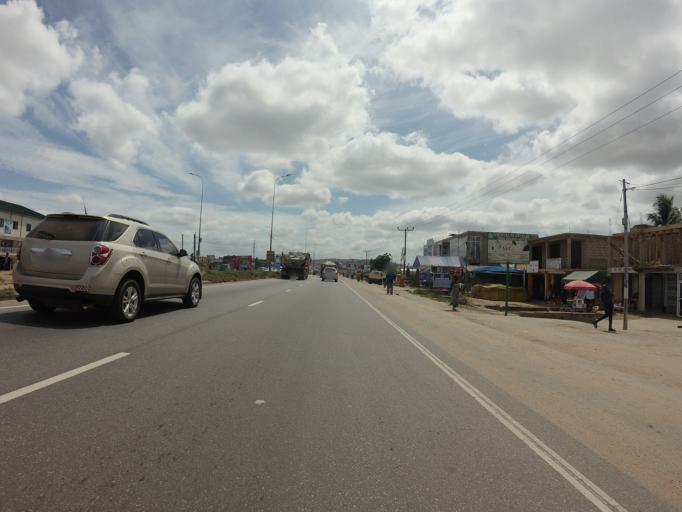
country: GH
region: Central
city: Kasoa
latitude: 5.5355
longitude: -0.4165
